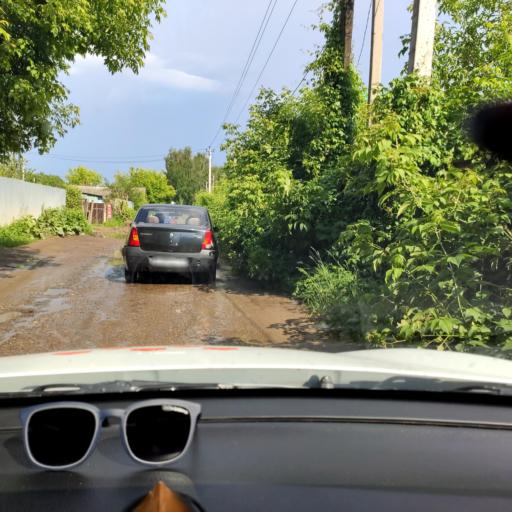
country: RU
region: Tatarstan
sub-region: Zelenodol'skiy Rayon
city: Vasil'yevo
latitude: 55.8275
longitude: 48.7591
